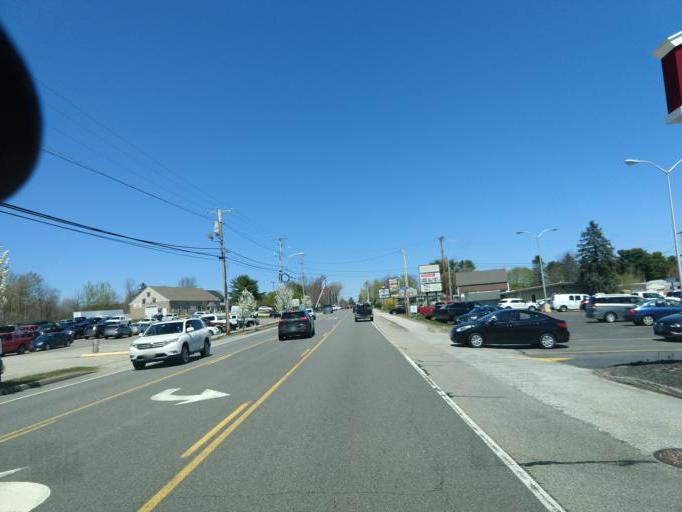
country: US
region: Maine
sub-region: York County
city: Wells Beach Station
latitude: 43.3085
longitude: -70.5846
